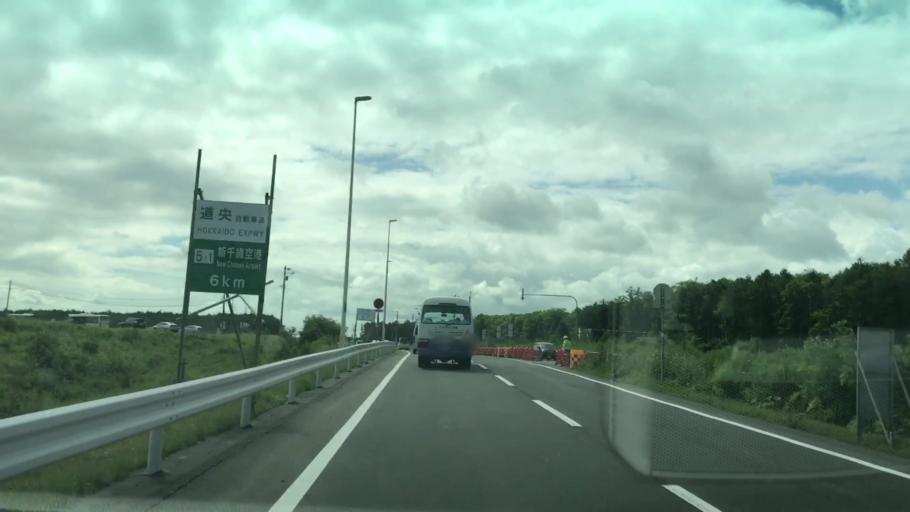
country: JP
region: Hokkaido
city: Chitose
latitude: 42.7734
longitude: 141.6790
